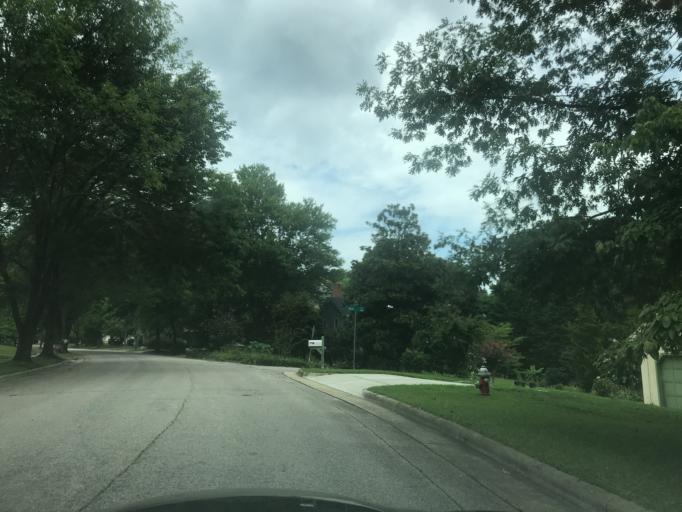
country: US
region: North Carolina
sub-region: Wake County
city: West Raleigh
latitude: 35.8927
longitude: -78.6128
